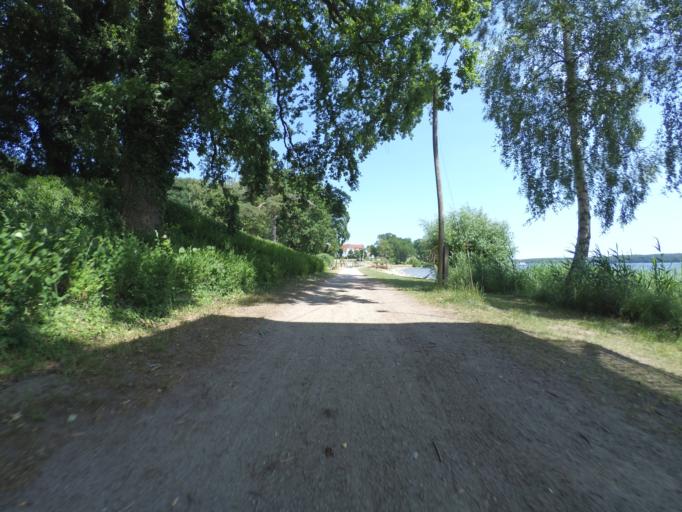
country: DE
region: Mecklenburg-Vorpommern
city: Plau am See
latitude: 53.4303
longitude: 12.2746
